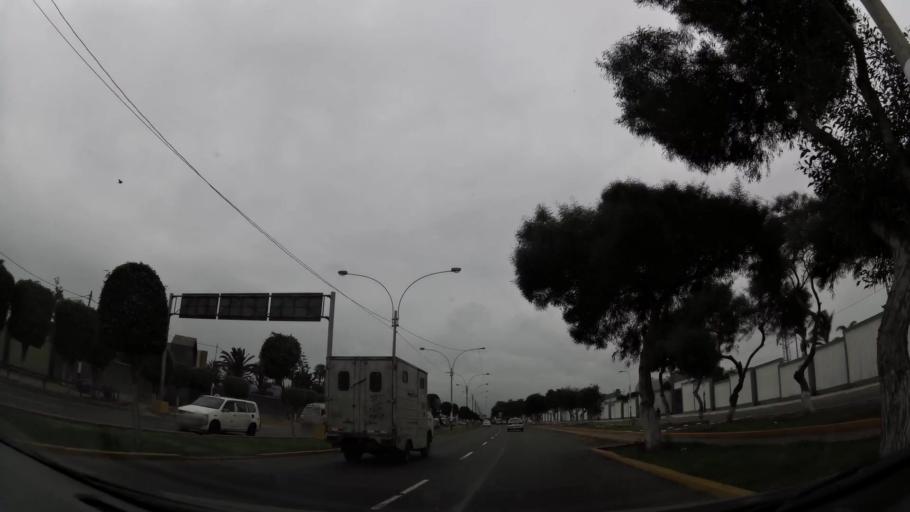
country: PE
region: Callao
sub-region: Callao
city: Callao
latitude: -12.0583
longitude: -77.1208
